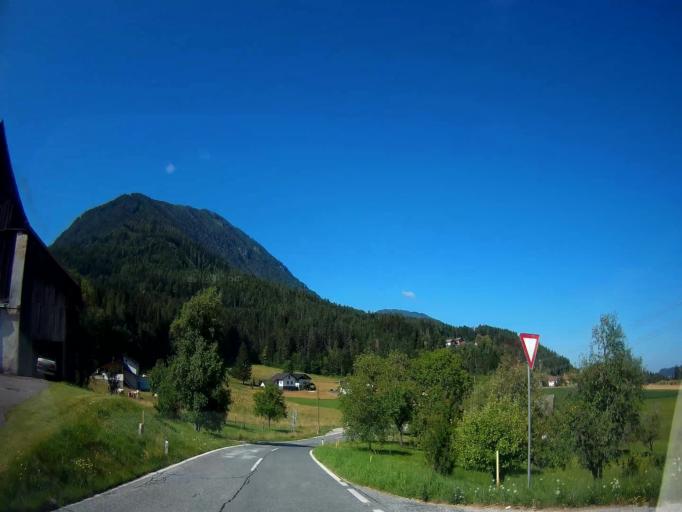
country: AT
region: Carinthia
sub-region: Politischer Bezirk Klagenfurt Land
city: Grafenstein
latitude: 46.5392
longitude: 14.4451
